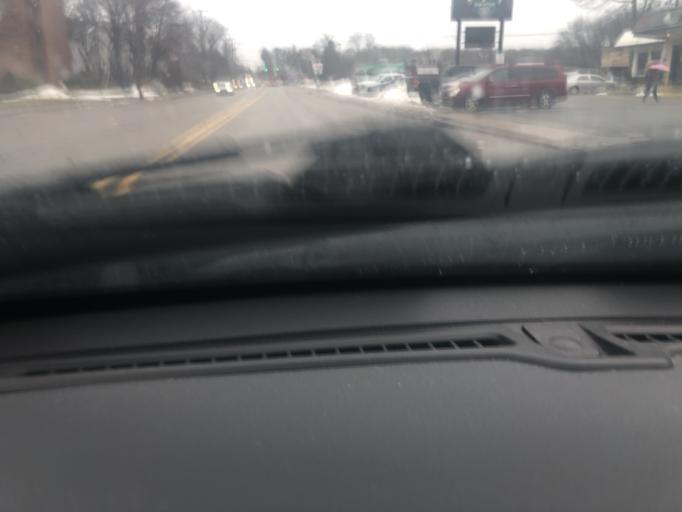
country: US
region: Massachusetts
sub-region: Norfolk County
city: Avon
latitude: 42.0999
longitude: -71.0649
